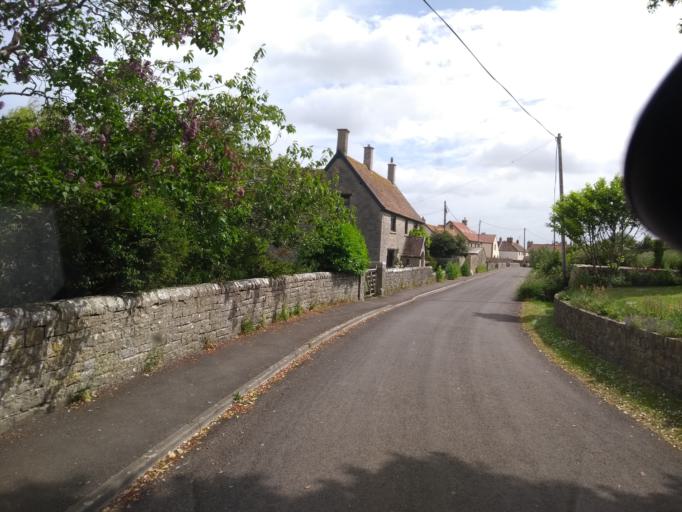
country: GB
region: England
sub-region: Somerset
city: Bridgwater
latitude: 51.1874
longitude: -3.0876
